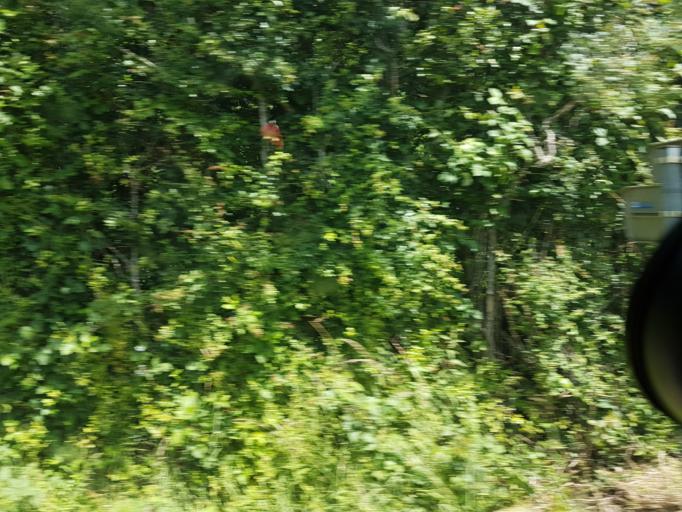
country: FR
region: Bourgogne
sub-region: Departement de Saone-et-Loire
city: Epinac
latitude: 47.0060
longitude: 4.4628
